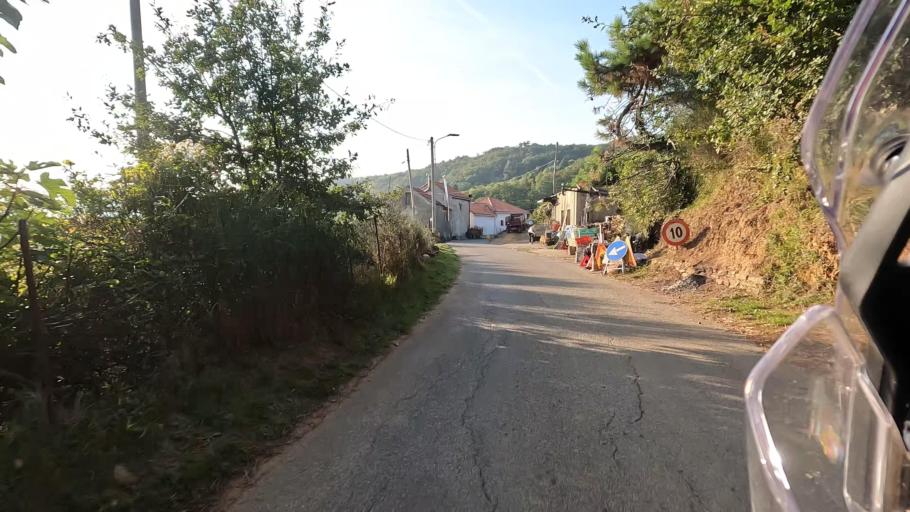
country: IT
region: Liguria
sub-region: Provincia di Savona
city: San Giovanni
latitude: 44.3935
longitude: 8.5281
